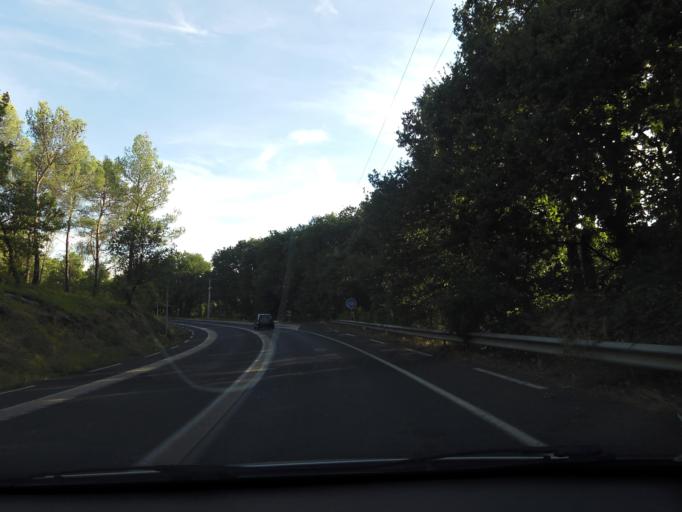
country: FR
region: Languedoc-Roussillon
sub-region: Departement de l'Herault
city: Montferrier-sur-Lez
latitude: 43.6670
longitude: 3.8667
